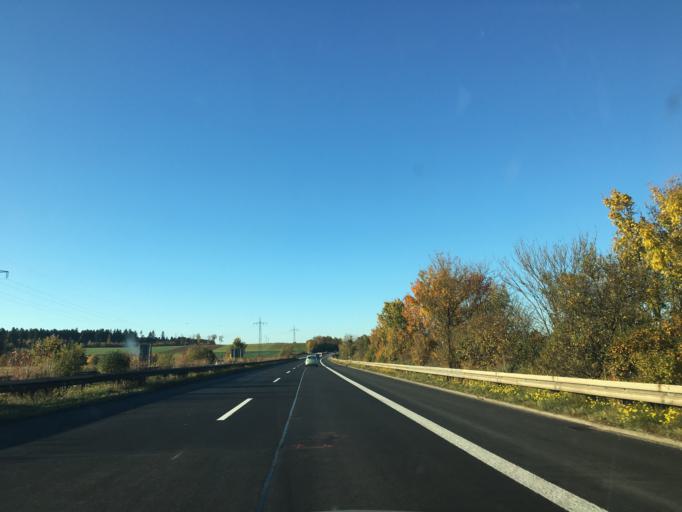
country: DE
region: Baden-Wuerttemberg
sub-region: Freiburg Region
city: Deisslingen
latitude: 48.1010
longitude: 8.5870
